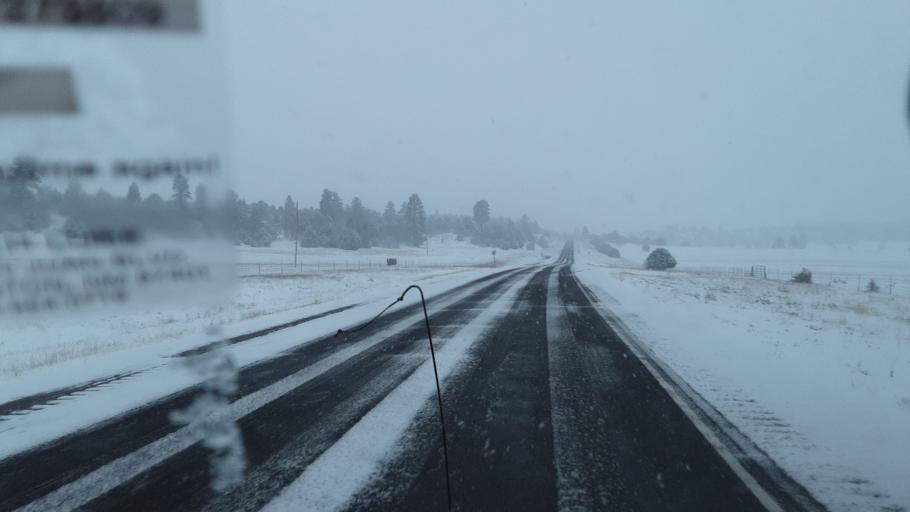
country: US
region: New Mexico
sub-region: Rio Arriba County
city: Dulce
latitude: 36.9186
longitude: -106.7979
